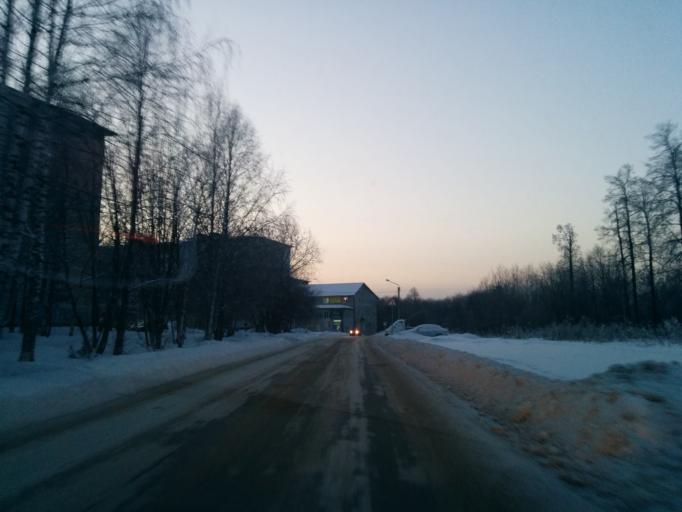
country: RU
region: Perm
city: Novyye Lyady
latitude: 58.0523
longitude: 56.5804
